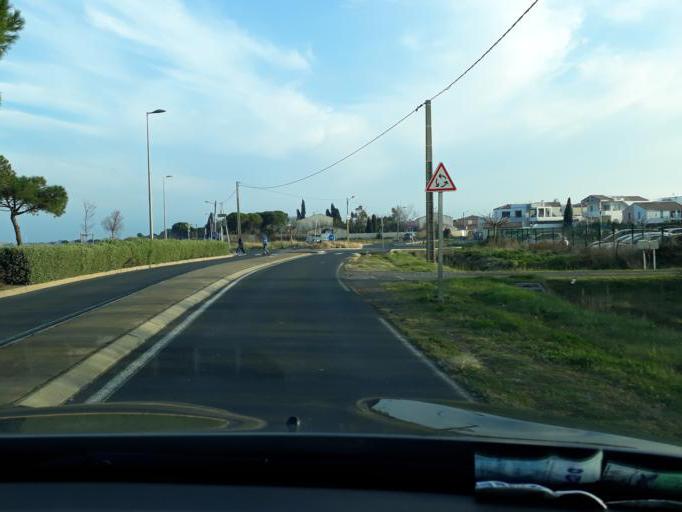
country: FR
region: Languedoc-Roussillon
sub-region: Departement de l'Herault
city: Marseillan
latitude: 43.3426
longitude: 3.5327
